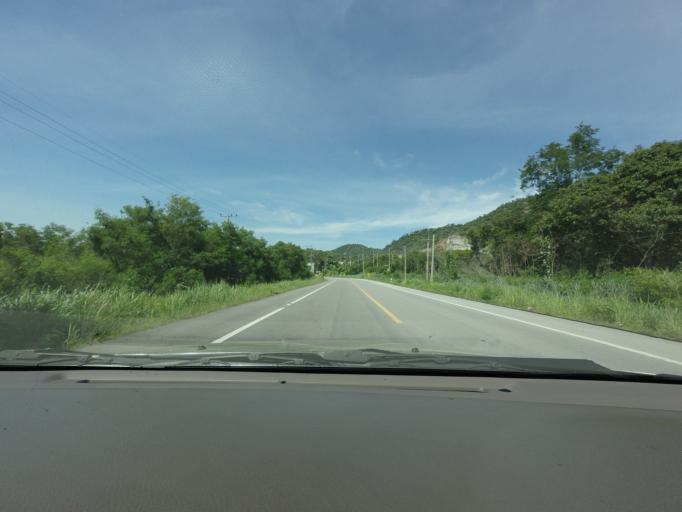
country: TH
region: Chon Buri
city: Si Racha
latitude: 13.2540
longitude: 100.9640
